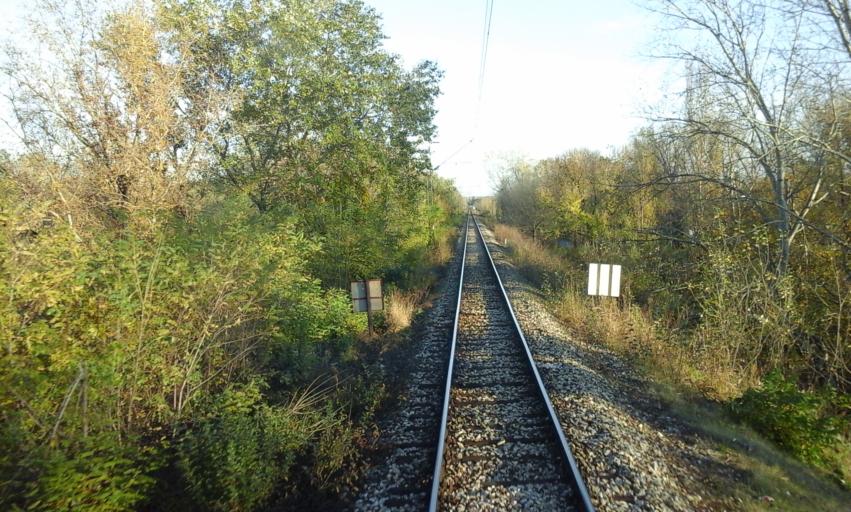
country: RS
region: Autonomna Pokrajina Vojvodina
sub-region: Juznobacki Okrug
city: Petrovaradin
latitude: 45.2593
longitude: 19.8659
